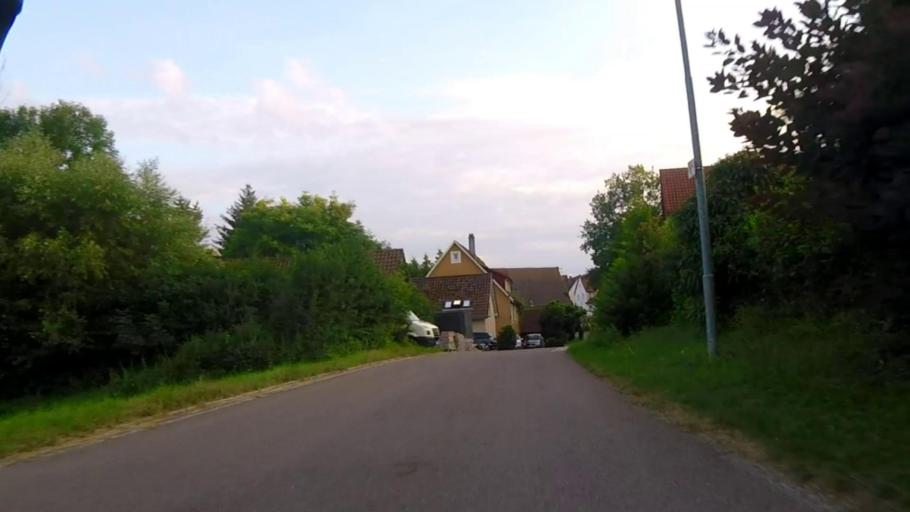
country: DE
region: Baden-Wuerttemberg
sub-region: Regierungsbezirk Stuttgart
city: Oberstenfeld
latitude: 49.0008
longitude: 9.3627
